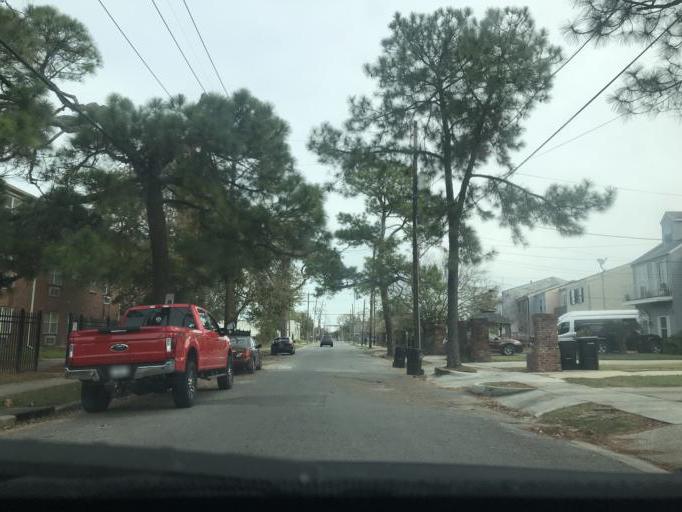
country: US
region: Louisiana
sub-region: Orleans Parish
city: New Orleans
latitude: 29.9574
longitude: -90.1123
